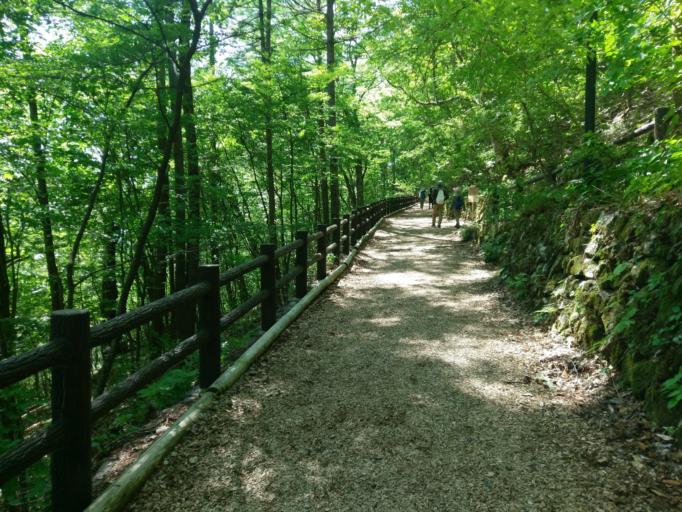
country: JP
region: Yamanashi
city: Uenohara
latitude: 35.7391
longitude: 139.0293
